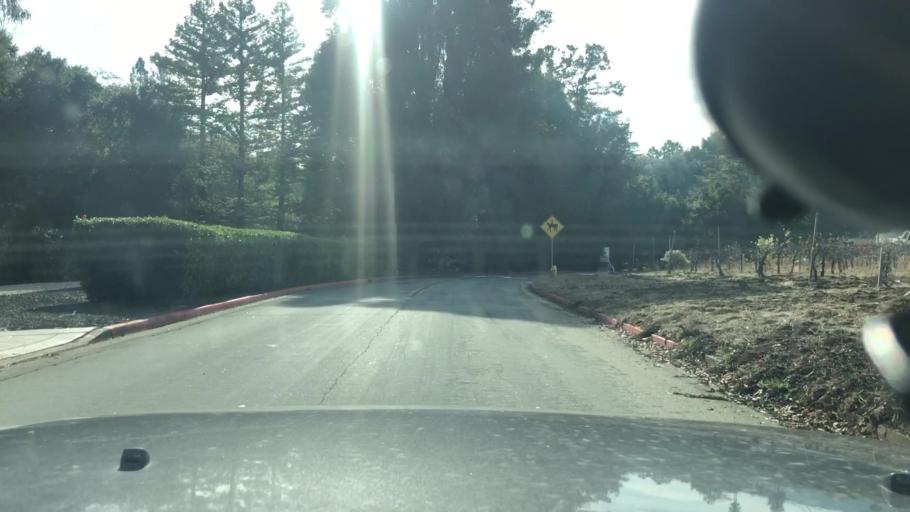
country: US
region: California
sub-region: Santa Clara County
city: Saratoga
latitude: 37.2653
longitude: -121.9995
